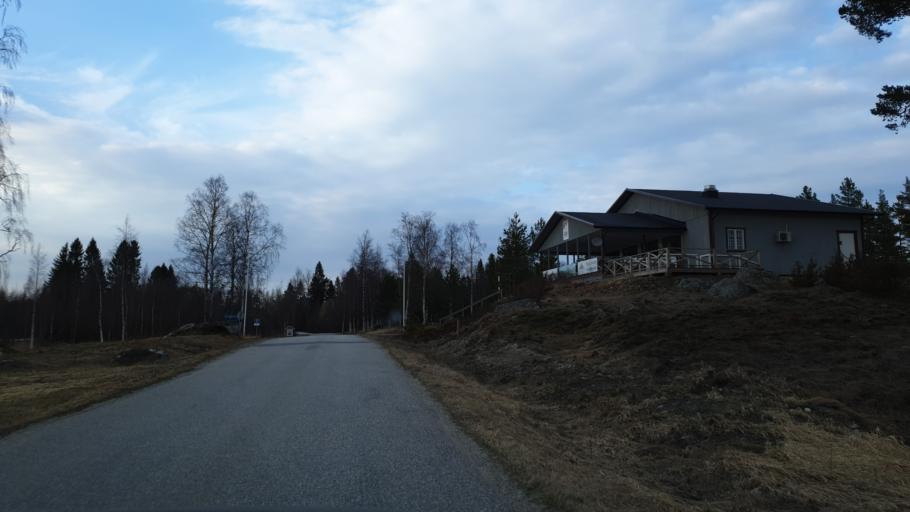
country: SE
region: Vaesternorrland
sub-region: Sundsvalls Kommun
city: Njurundabommen
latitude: 62.0204
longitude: 17.4072
